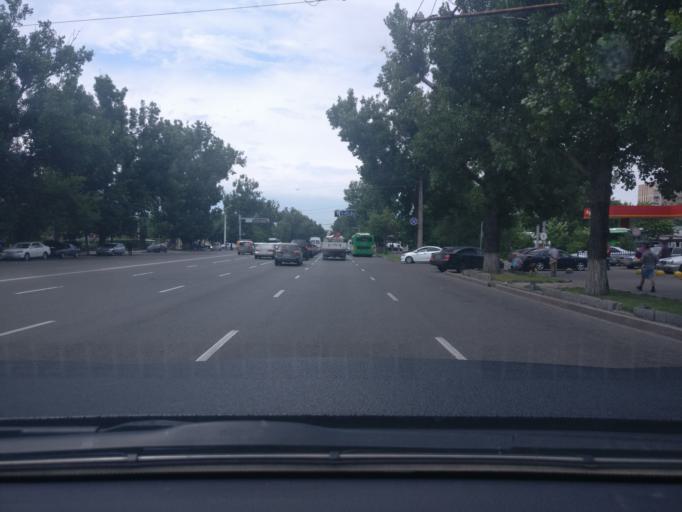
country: KZ
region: Almaty Qalasy
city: Almaty
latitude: 43.2446
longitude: 76.8567
